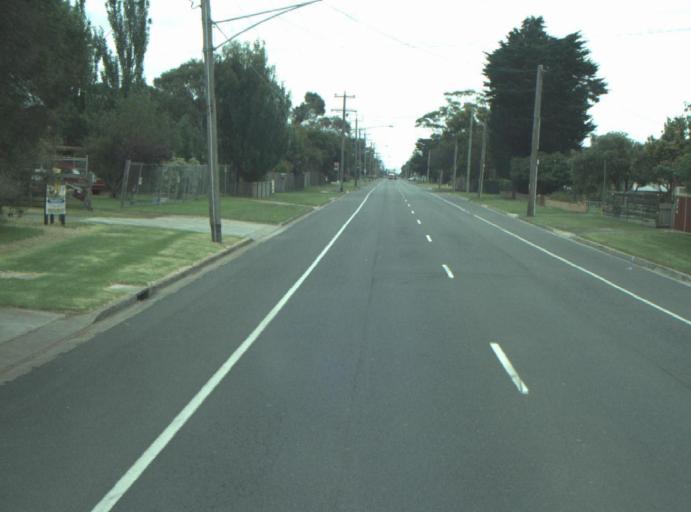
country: AU
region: Victoria
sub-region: Greater Geelong
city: East Geelong
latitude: -38.1715
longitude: 144.4029
